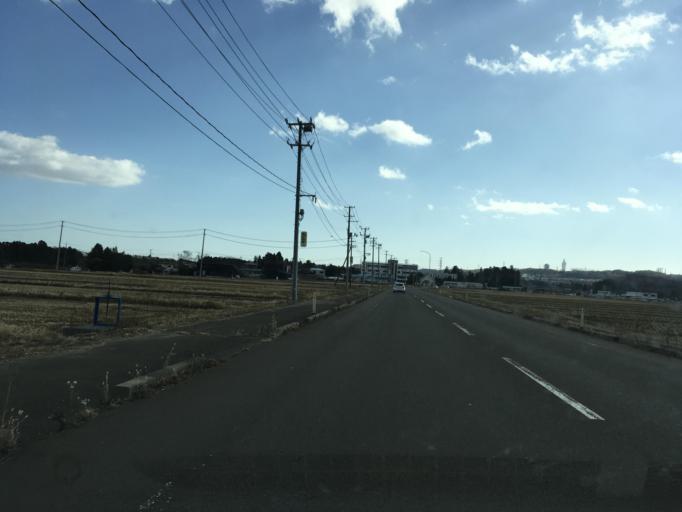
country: JP
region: Miyagi
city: Sendai-shi
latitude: 38.3360
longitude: 140.7987
